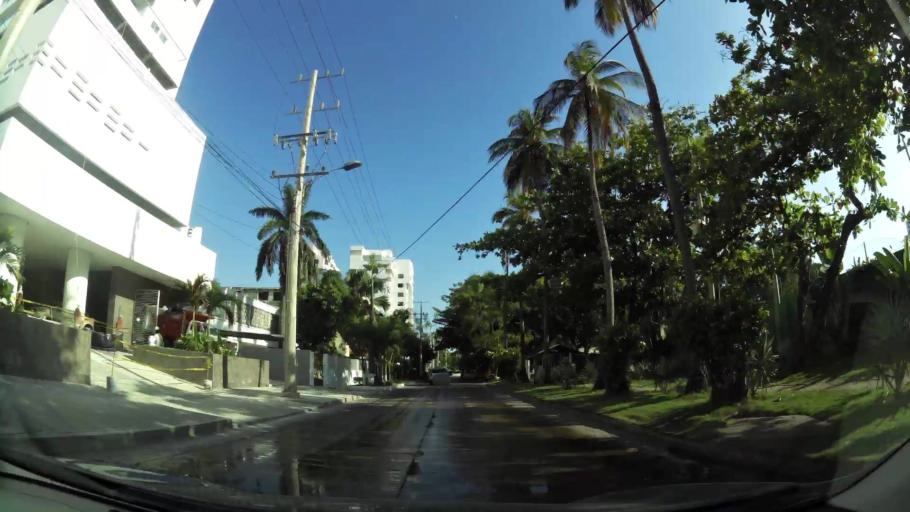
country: CO
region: Bolivar
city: Cartagena
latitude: 10.3971
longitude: -75.5591
